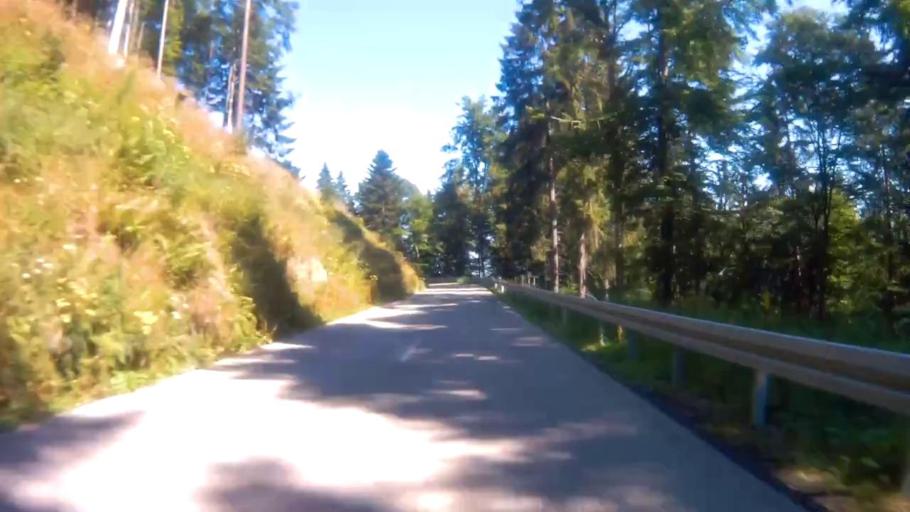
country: DE
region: Baden-Wuerttemberg
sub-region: Freiburg Region
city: Badenweiler
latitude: 47.7865
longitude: 7.7074
